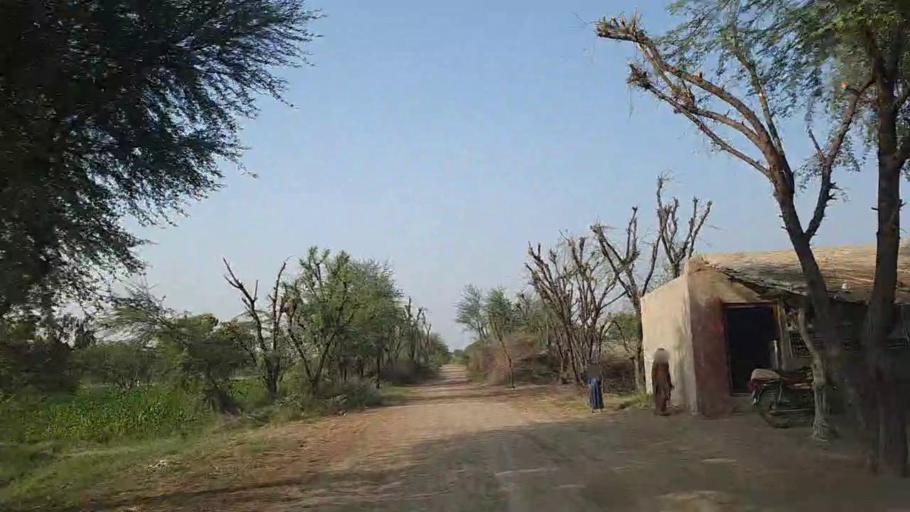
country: PK
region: Sindh
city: Dhoro Naro
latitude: 25.4957
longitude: 69.4997
